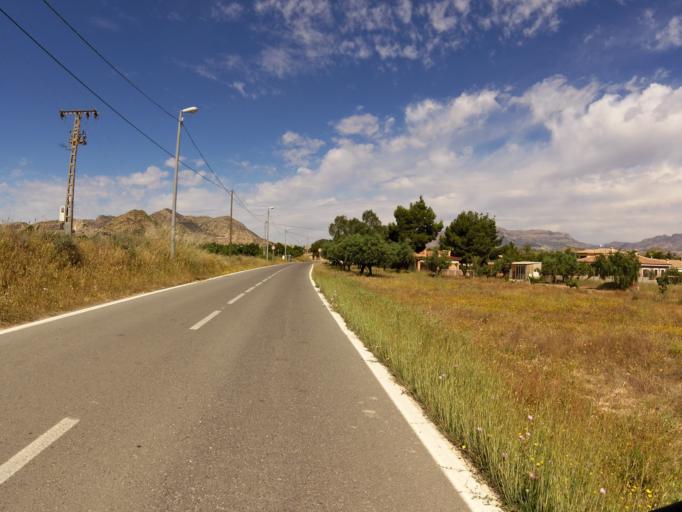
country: ES
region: Valencia
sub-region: Provincia de Alicante
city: Agost
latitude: 38.3952
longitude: -0.5962
